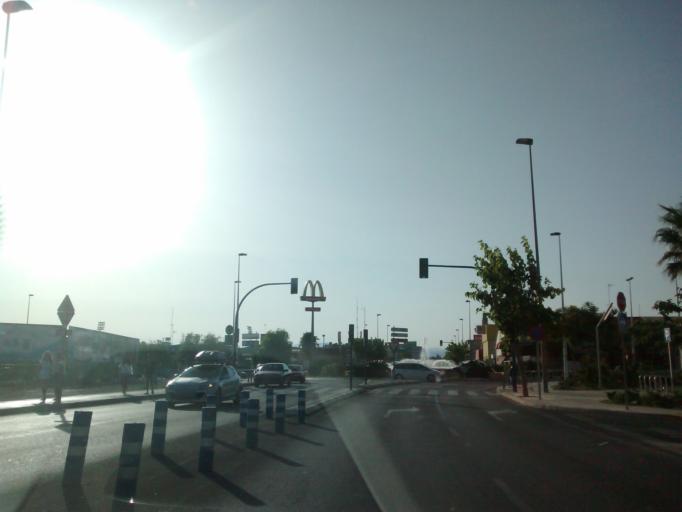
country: ES
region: Valencia
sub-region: Provincia de Alicante
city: Santa Pola
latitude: 38.1967
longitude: -0.5620
